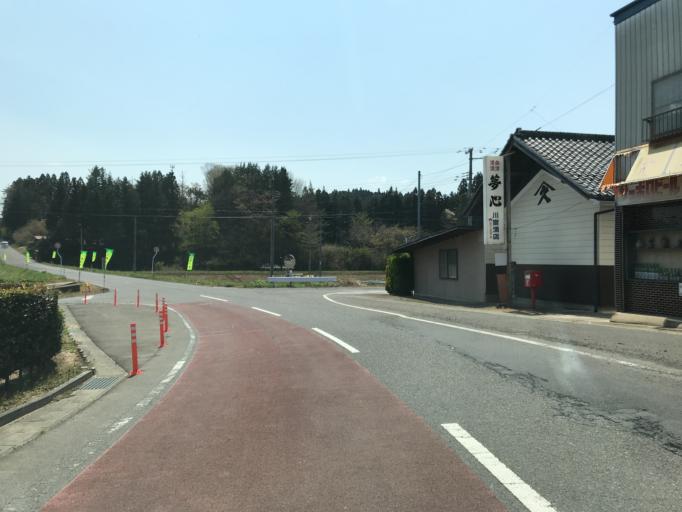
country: JP
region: Fukushima
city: Ishikawa
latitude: 37.0980
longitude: 140.4069
